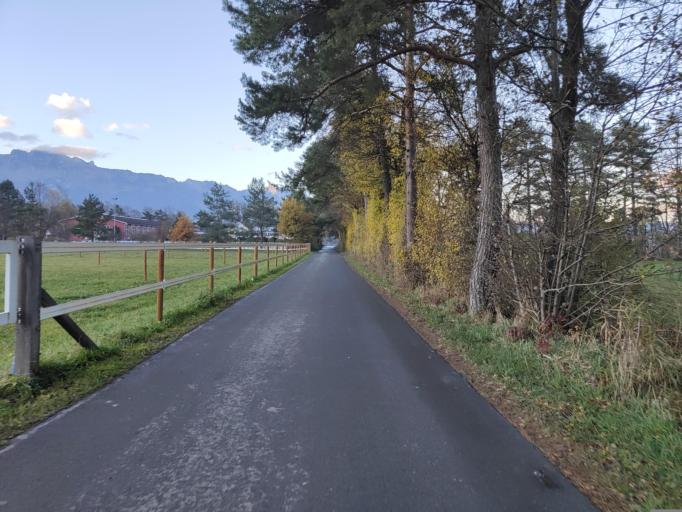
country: LI
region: Planken
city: Planken
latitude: 47.1904
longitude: 9.5248
